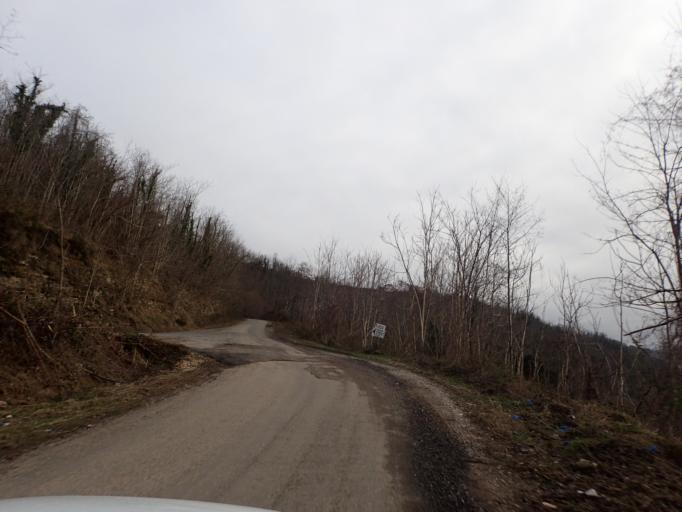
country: TR
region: Ordu
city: Camas
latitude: 40.9411
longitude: 37.5154
